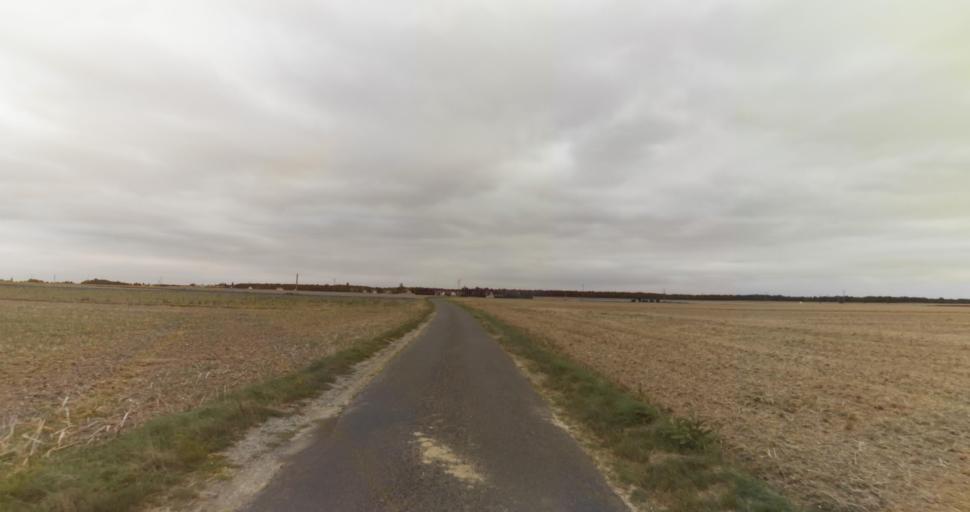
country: FR
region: Haute-Normandie
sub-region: Departement de l'Eure
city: La Couture-Boussey
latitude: 48.9190
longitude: 1.3923
